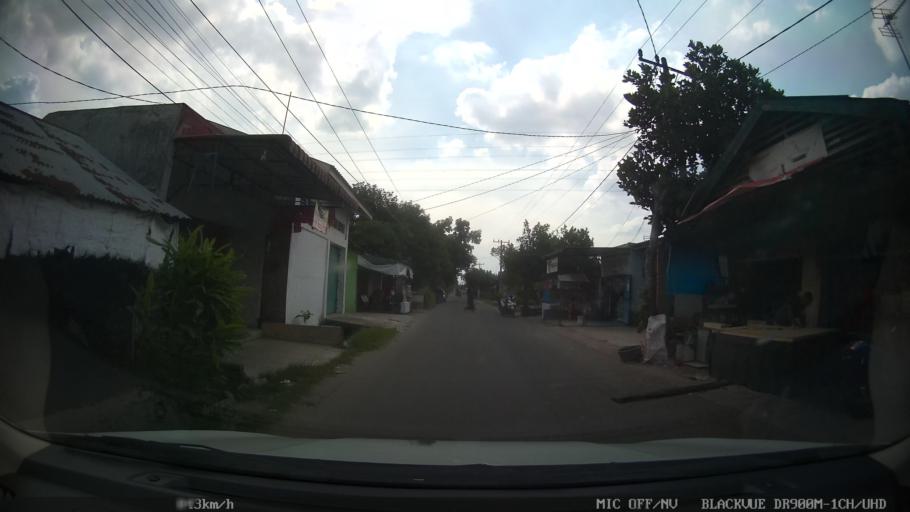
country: ID
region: North Sumatra
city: Binjai
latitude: 3.6352
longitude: 98.5074
